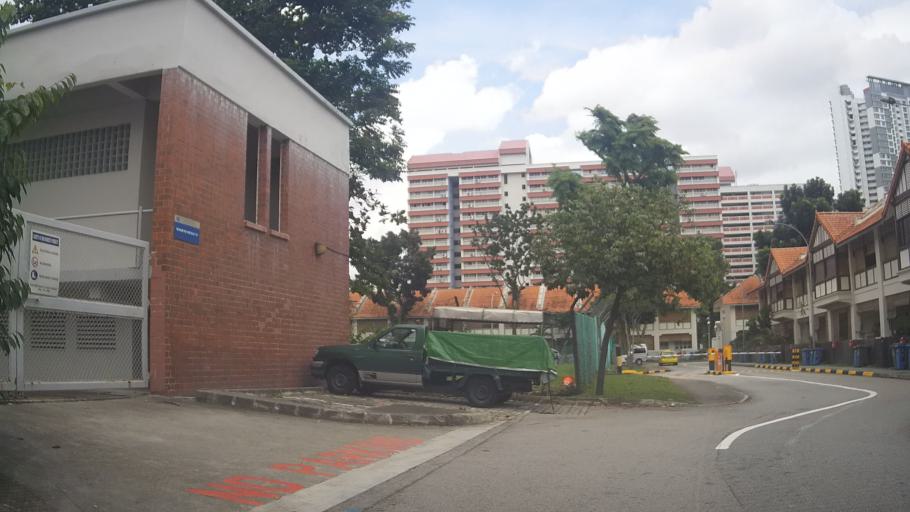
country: SG
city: Singapore
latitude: 1.3198
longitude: 103.8575
